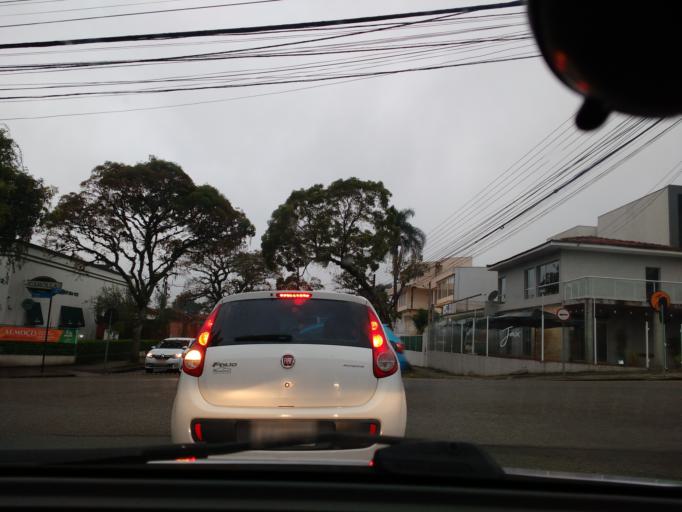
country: BR
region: Parana
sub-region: Curitiba
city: Curitiba
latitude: -25.4234
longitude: -49.2432
